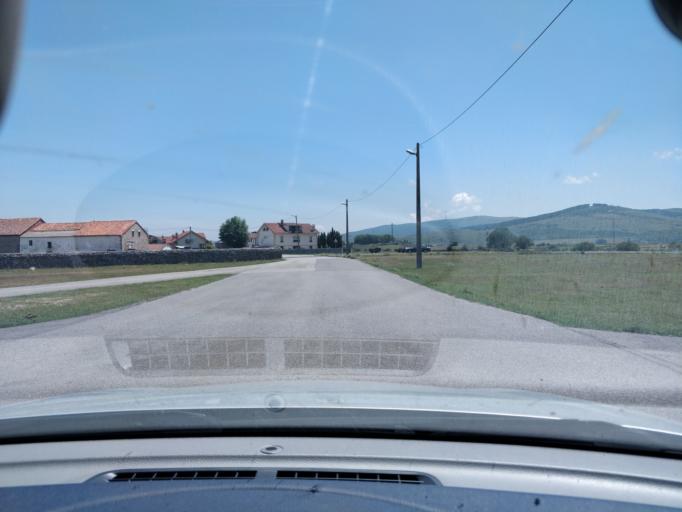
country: ES
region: Cantabria
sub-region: Provincia de Cantabria
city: Reinosa
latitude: 42.9976
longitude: -4.1563
